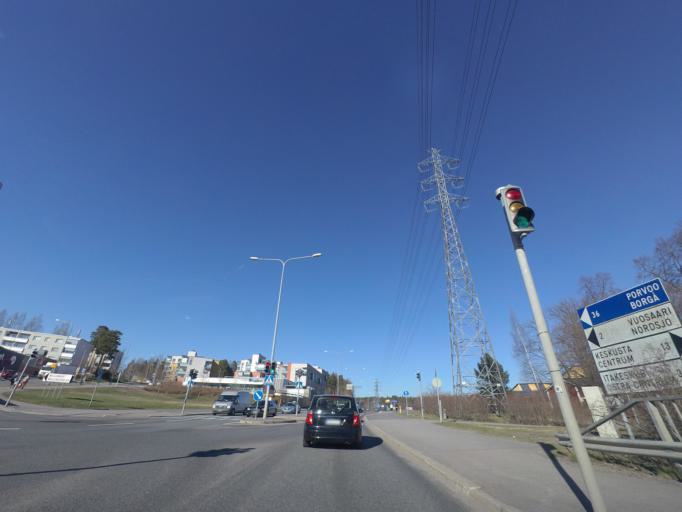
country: FI
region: Uusimaa
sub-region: Helsinki
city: Vantaa
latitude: 60.2307
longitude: 25.1278
